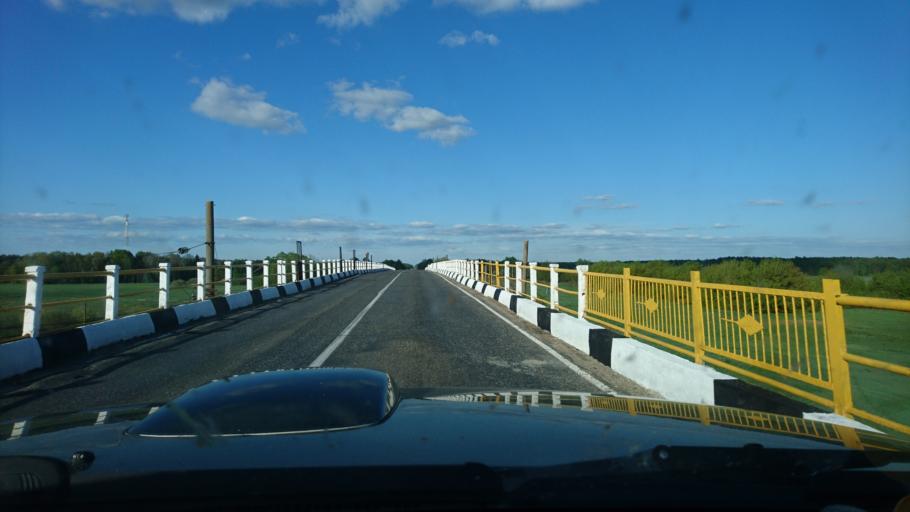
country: BY
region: Brest
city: Nyakhachava
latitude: 52.6385
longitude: 25.1945
